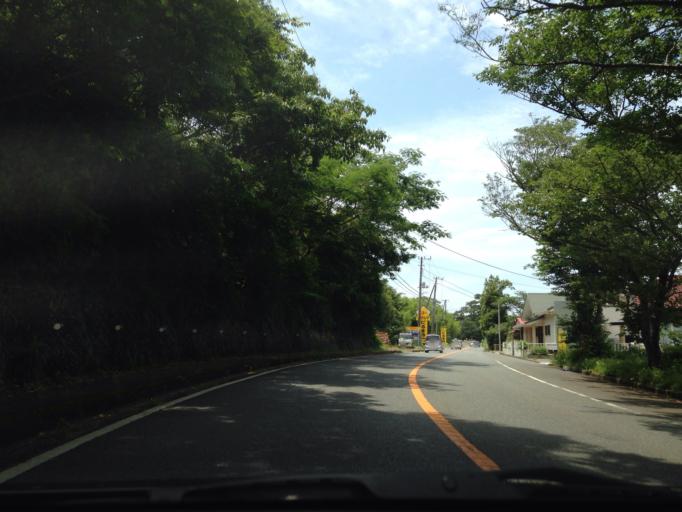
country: JP
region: Shizuoka
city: Heda
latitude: 34.8741
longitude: 138.7625
